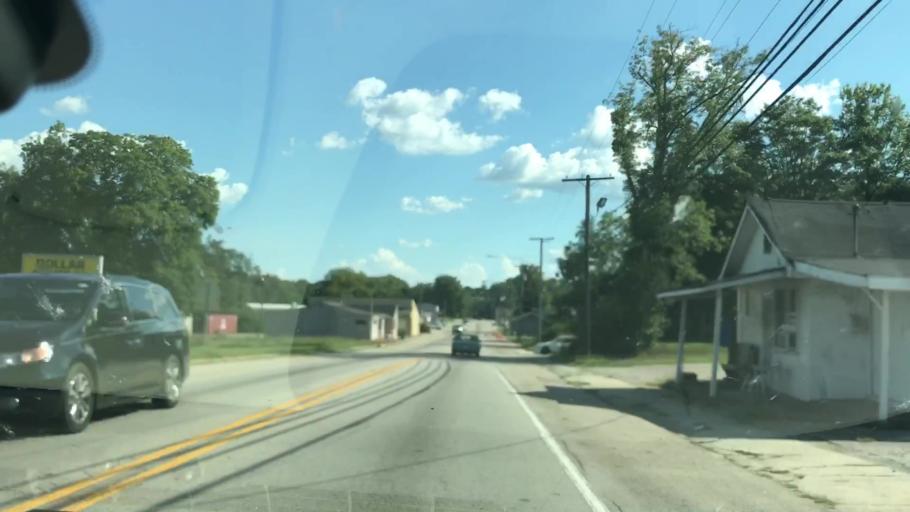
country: US
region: Georgia
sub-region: Troup County
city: La Grange
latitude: 33.0281
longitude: -85.0238
